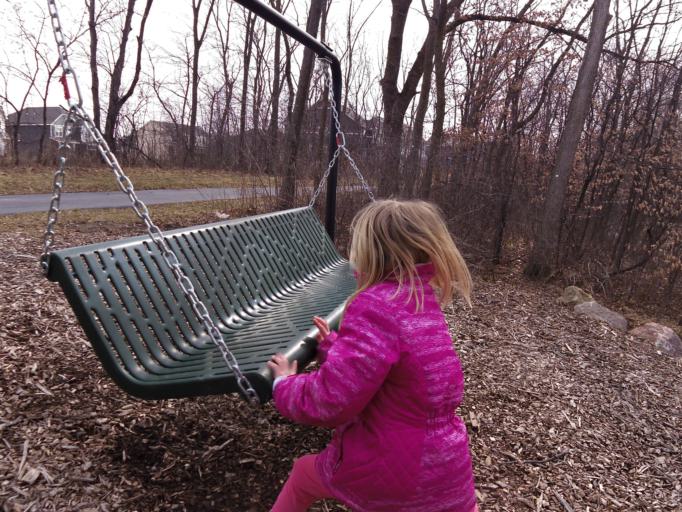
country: US
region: Minnesota
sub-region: Scott County
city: Prior Lake
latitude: 44.6964
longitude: -93.4479
